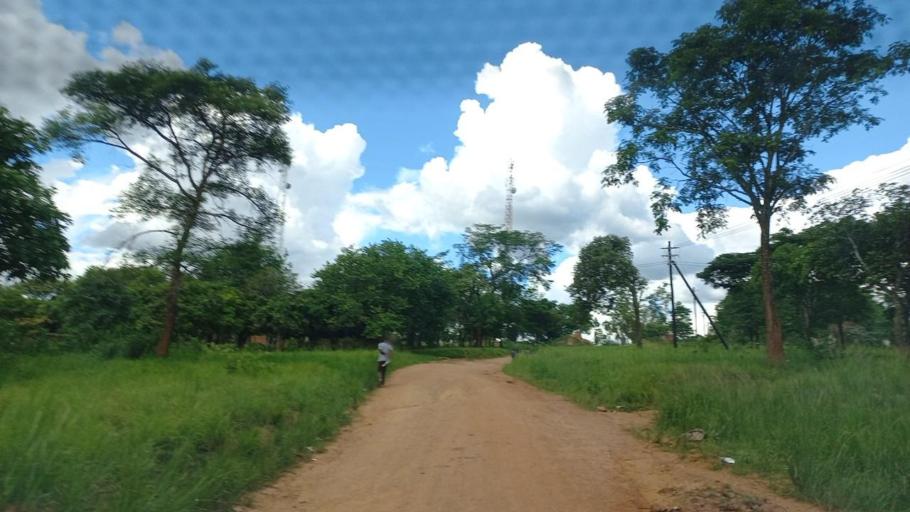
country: ZM
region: North-Western
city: Mwinilunga
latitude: -12.0692
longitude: 24.3013
